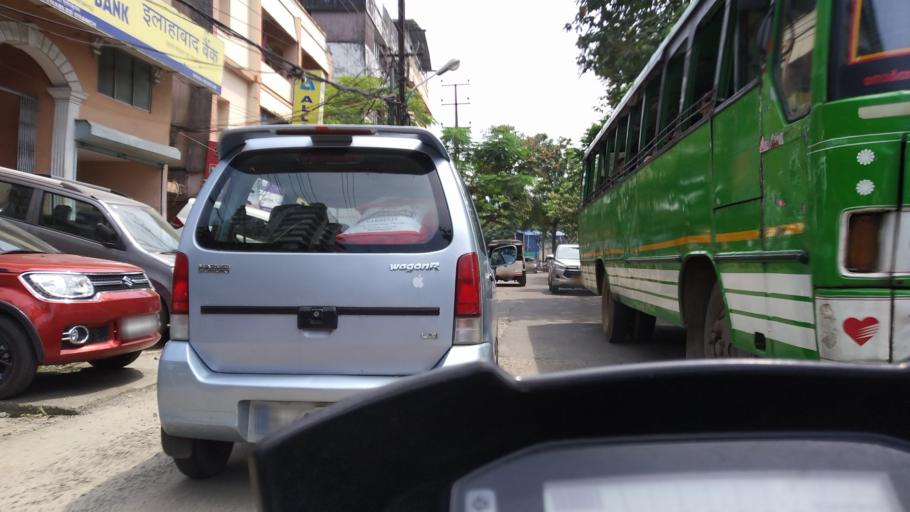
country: IN
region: Kerala
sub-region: Ernakulam
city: Cochin
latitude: 9.9614
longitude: 76.2869
